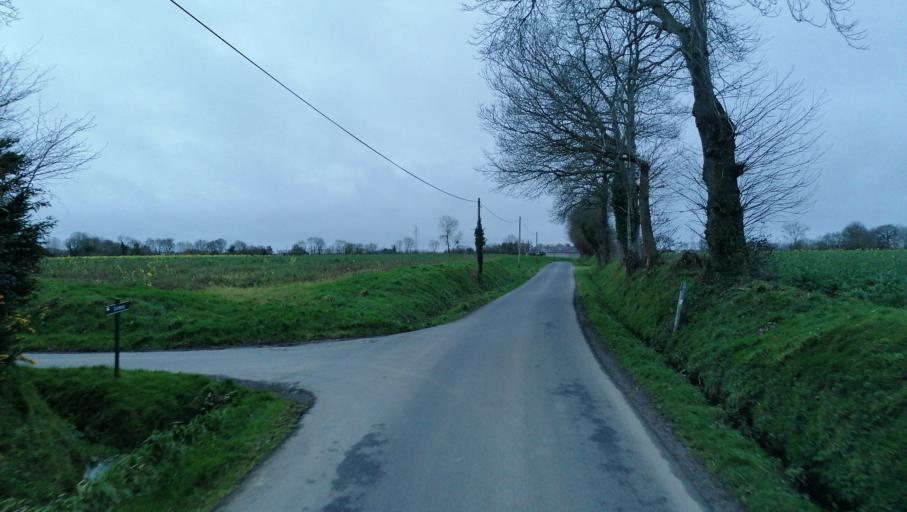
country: FR
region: Brittany
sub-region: Departement des Cotes-d'Armor
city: Goudelin
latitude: 48.5728
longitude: -3.0544
